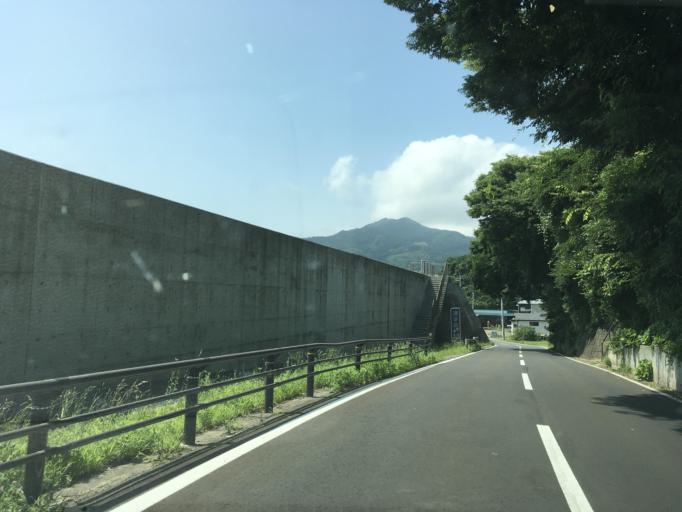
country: JP
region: Iwate
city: Ofunato
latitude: 38.9970
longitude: 141.7215
